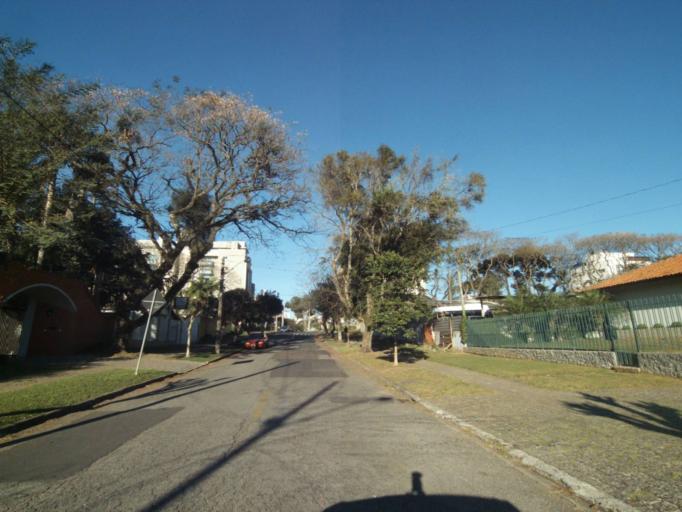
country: BR
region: Parana
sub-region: Curitiba
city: Curitiba
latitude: -25.4594
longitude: -49.2984
